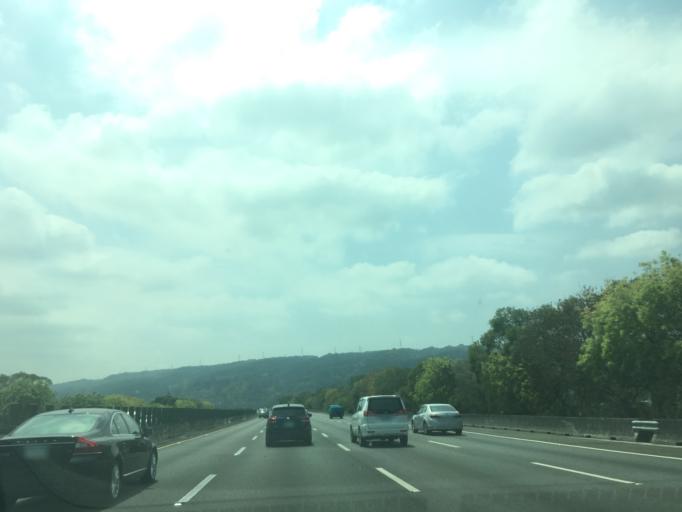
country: TW
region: Taiwan
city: Zhongxing New Village
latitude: 23.9767
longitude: 120.6504
